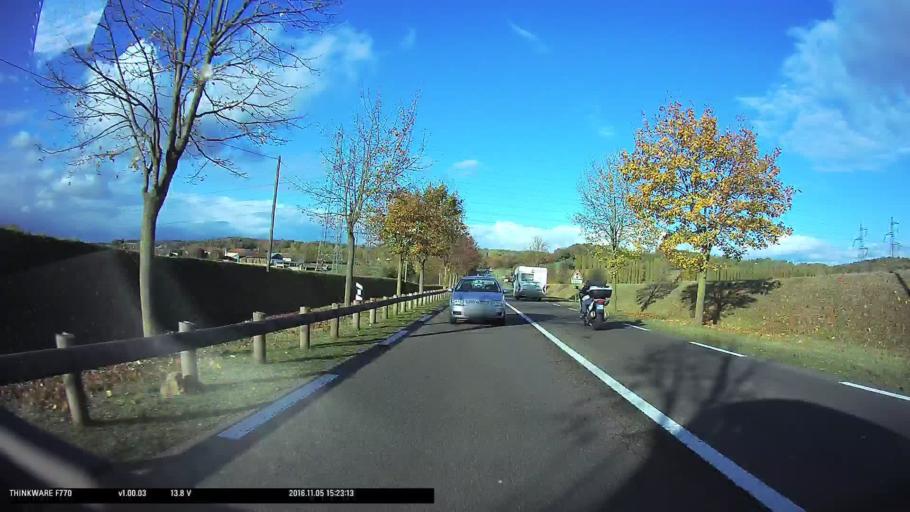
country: FR
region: Ile-de-France
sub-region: Departement du Val-d'Oise
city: Sagy
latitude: 49.0460
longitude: 1.9553
